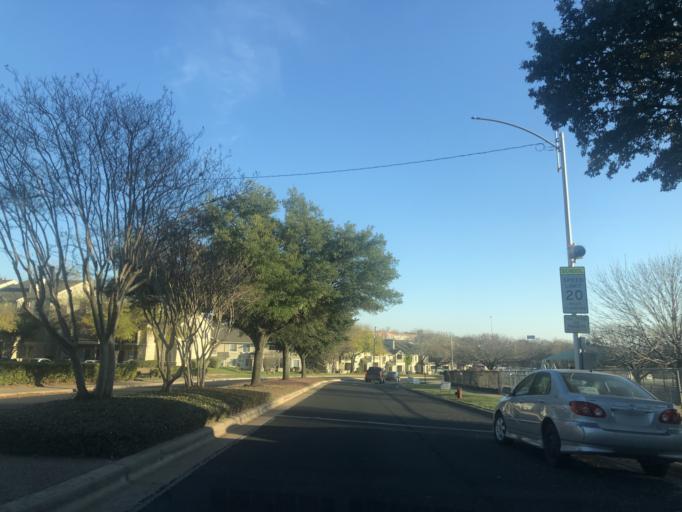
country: US
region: Texas
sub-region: Travis County
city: Wells Branch
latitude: 30.4329
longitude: -97.6759
